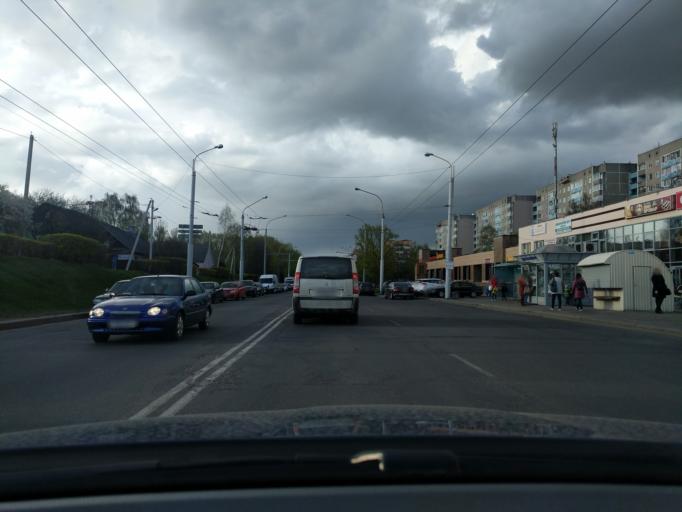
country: BY
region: Minsk
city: Novoye Medvezhino
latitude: 53.8946
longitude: 27.4813
